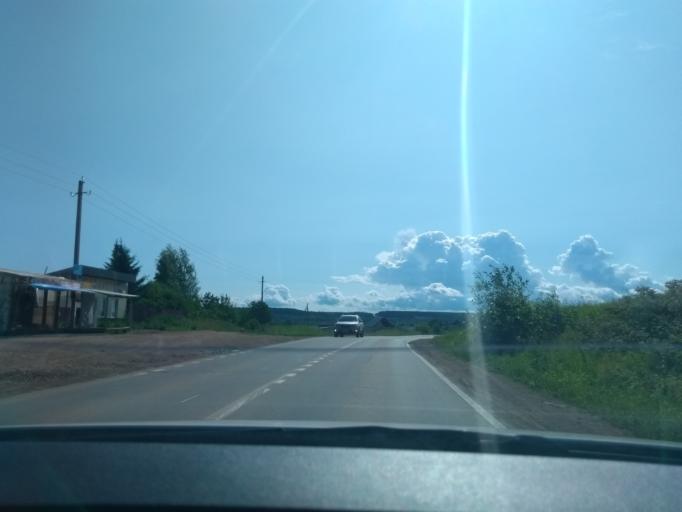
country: RU
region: Perm
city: Lobanovo
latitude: 57.8521
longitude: 56.3334
